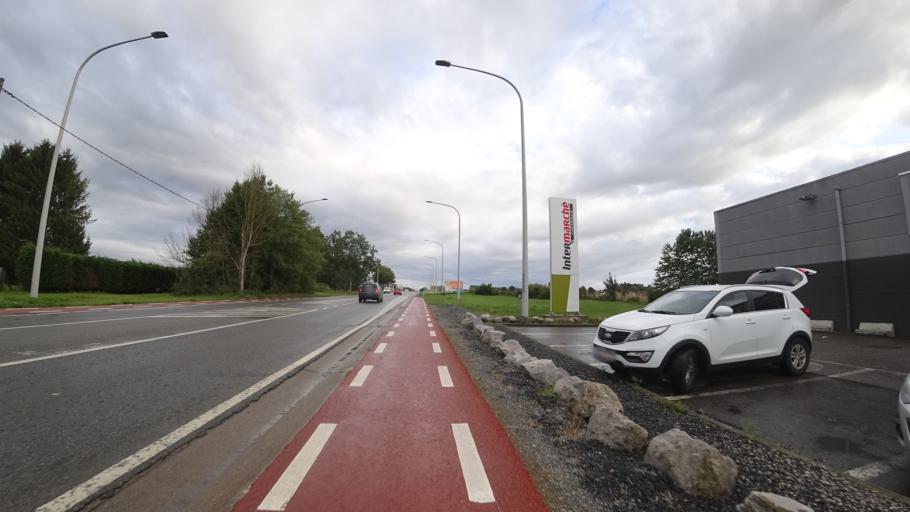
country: BE
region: Wallonia
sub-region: Province du Brabant Wallon
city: Chastre-Villeroux-Blanmont
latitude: 50.6387
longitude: 4.6494
